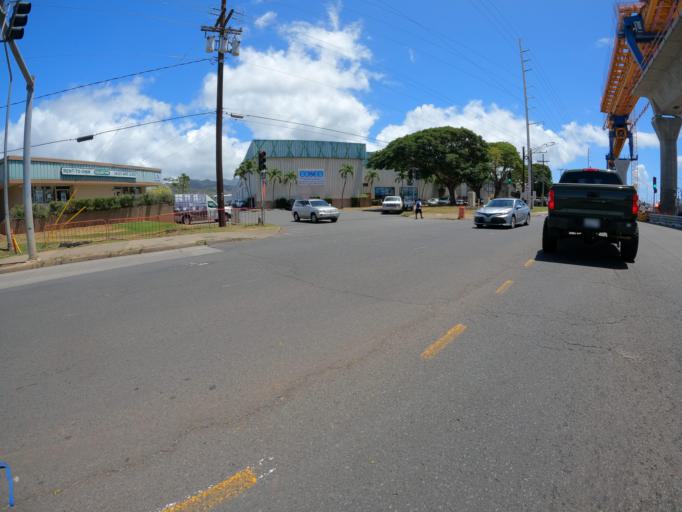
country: US
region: Hawaii
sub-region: Honolulu County
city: Honolulu
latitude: 21.3326
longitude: -157.8874
